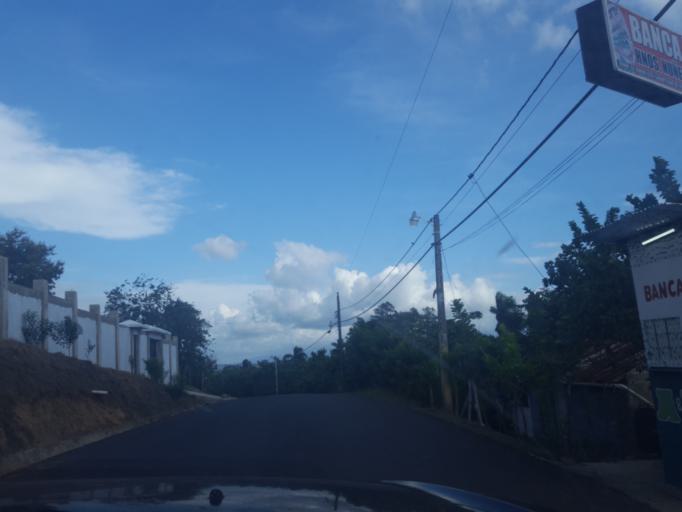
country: DO
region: La Vega
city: Rio Verde Arriba
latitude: 19.3522
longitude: -70.6284
